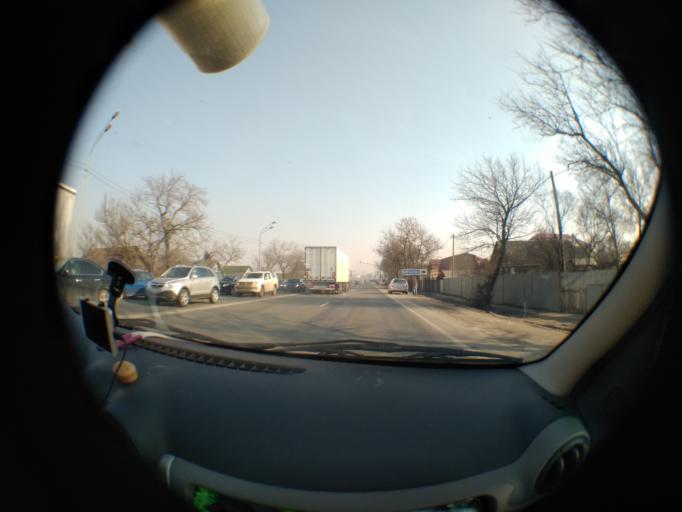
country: RU
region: Moskovskaya
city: Ostrovtsy
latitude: 55.5858
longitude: 38.0103
